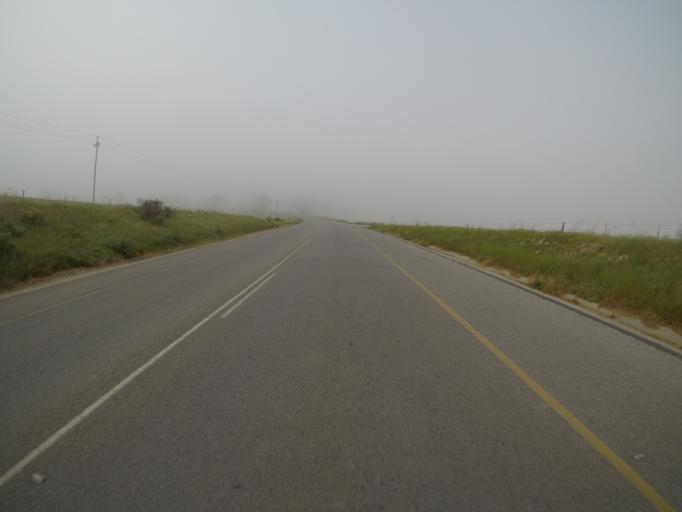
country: ZA
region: Western Cape
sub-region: City of Cape Town
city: Kraaifontein
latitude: -33.6914
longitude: 18.7039
